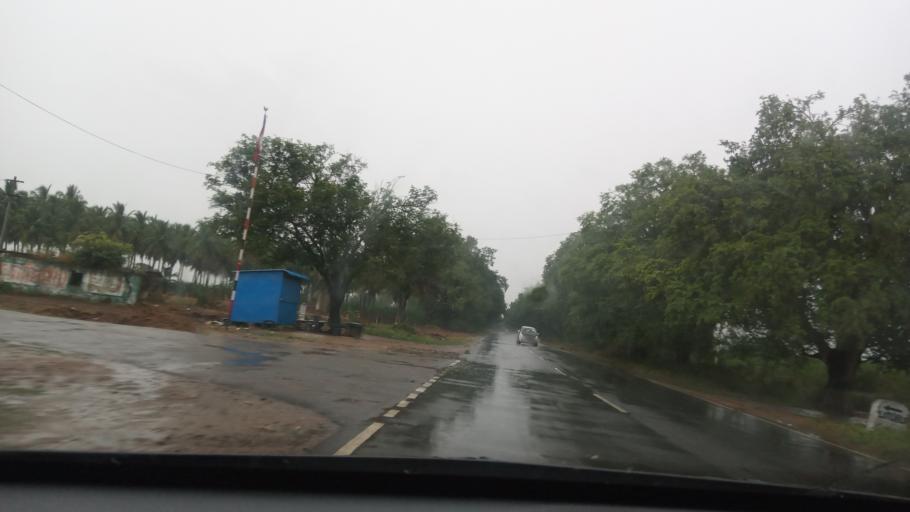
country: IN
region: Tamil Nadu
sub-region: Vellore
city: Kalavai
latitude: 12.8449
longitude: 79.3966
